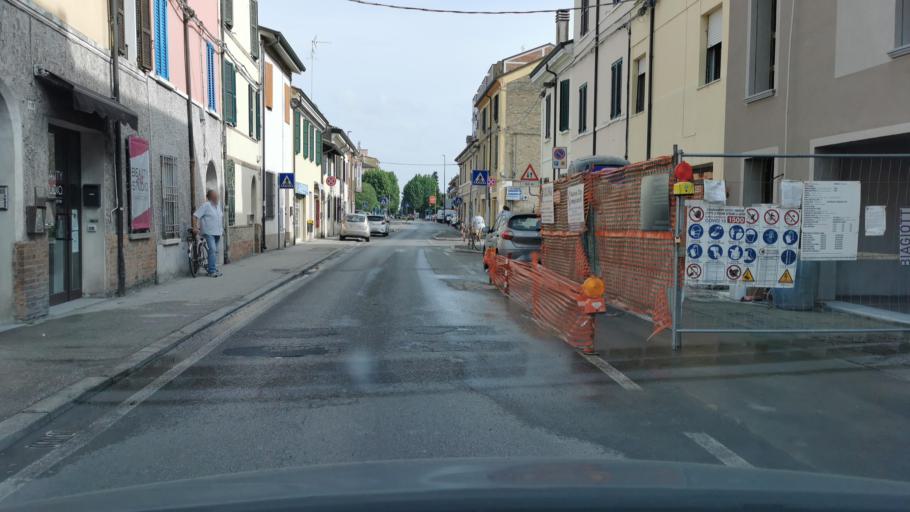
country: IT
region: Emilia-Romagna
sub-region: Provincia di Ravenna
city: Ravenna
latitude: 44.4101
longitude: 12.2073
